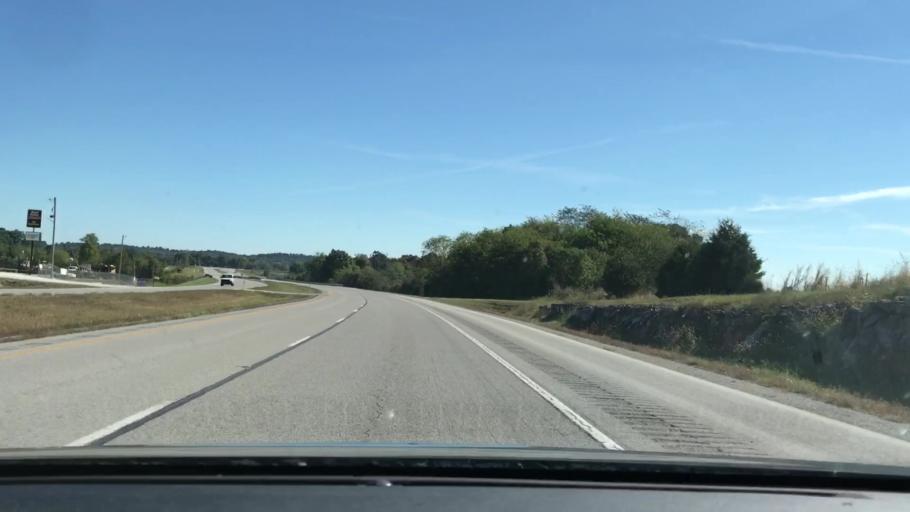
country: US
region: Kentucky
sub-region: Todd County
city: Elkton
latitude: 36.8212
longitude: -87.1722
